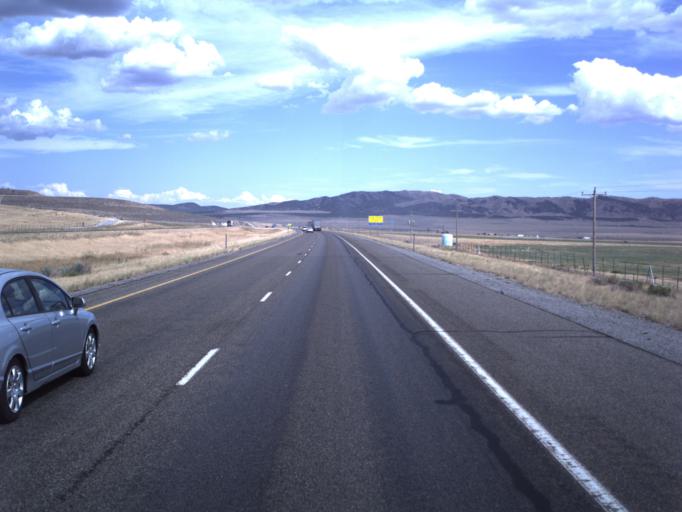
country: US
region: Idaho
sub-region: Oneida County
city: Malad City
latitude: 41.9749
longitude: -112.7885
